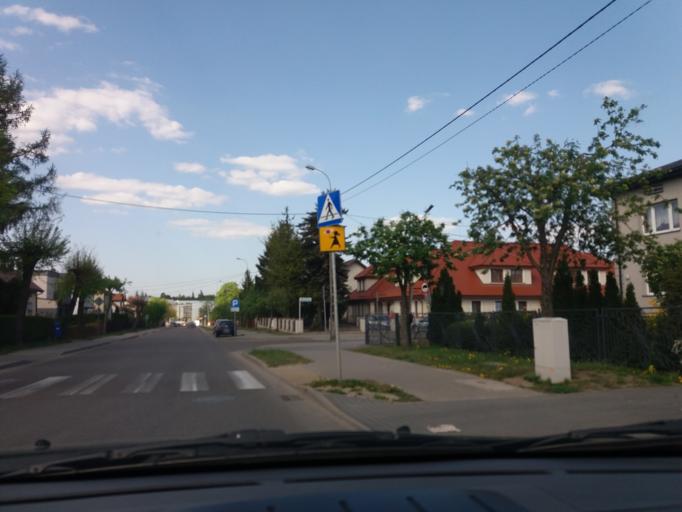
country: PL
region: Masovian Voivodeship
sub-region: Powiat mlawski
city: Mlawa
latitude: 53.1176
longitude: 20.3677
